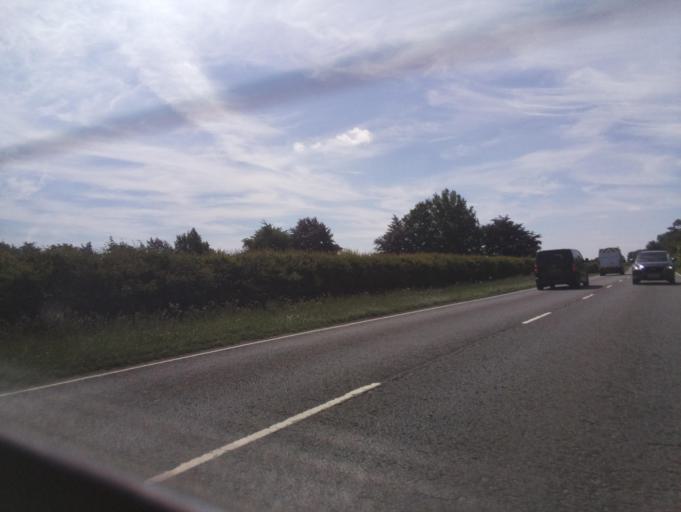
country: GB
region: England
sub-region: Lincolnshire
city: Burton
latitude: 53.3698
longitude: -0.5460
